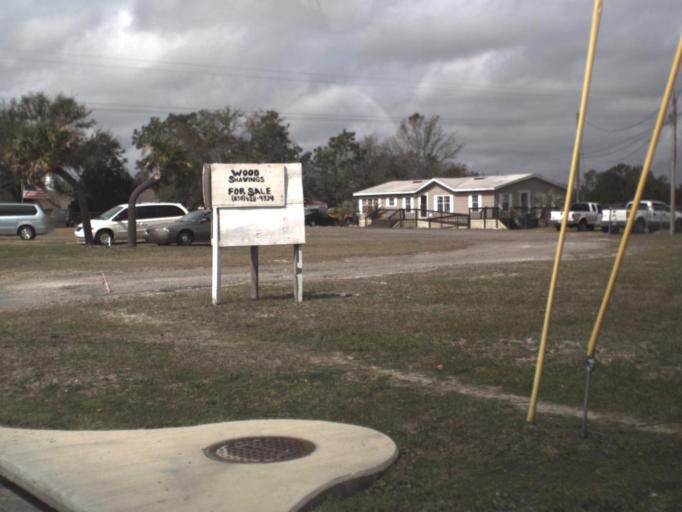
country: US
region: Florida
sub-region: Bay County
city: Cedar Grove
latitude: 30.1750
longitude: -85.6087
